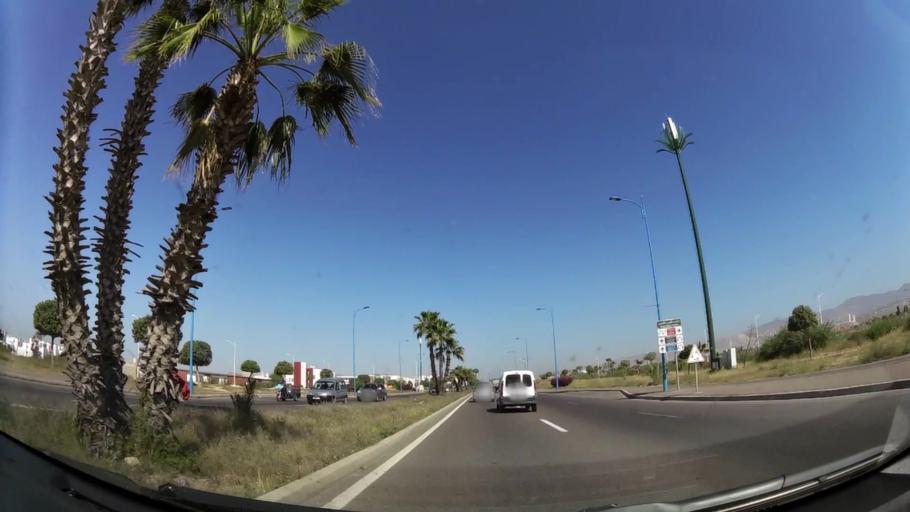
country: MA
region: Oued ed Dahab-Lagouira
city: Dakhla
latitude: 30.4092
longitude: -9.5392
